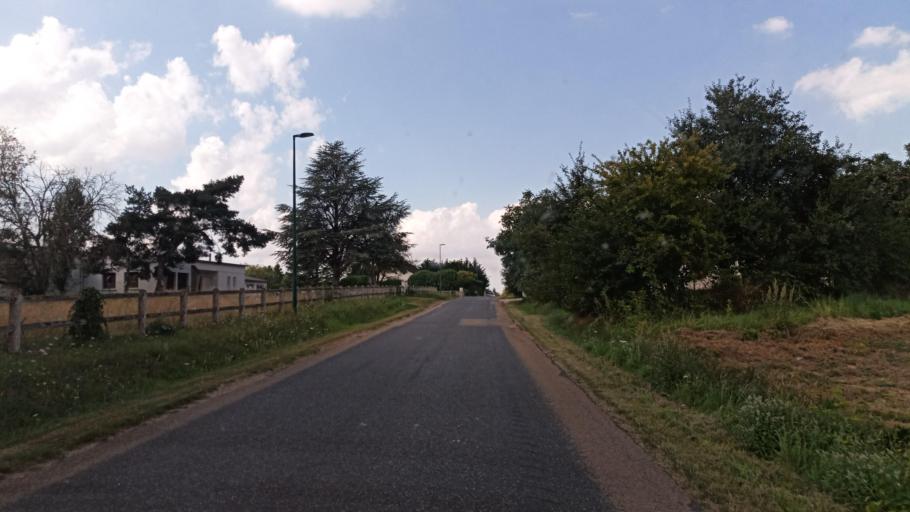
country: FR
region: Bourgogne
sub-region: Departement de l'Yonne
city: Egriselles-le-Bocage
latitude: 48.0521
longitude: 3.1516
